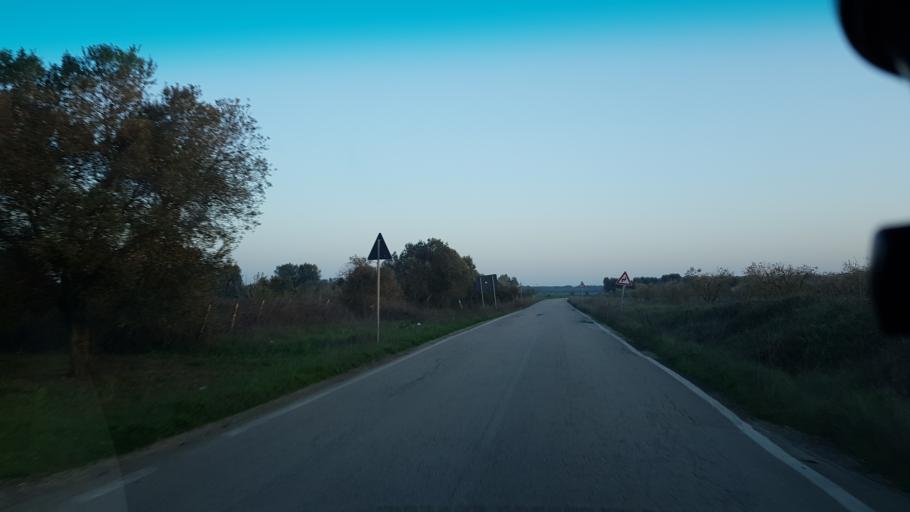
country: IT
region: Apulia
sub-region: Provincia di Brindisi
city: Mesagne
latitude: 40.6184
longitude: 17.7854
